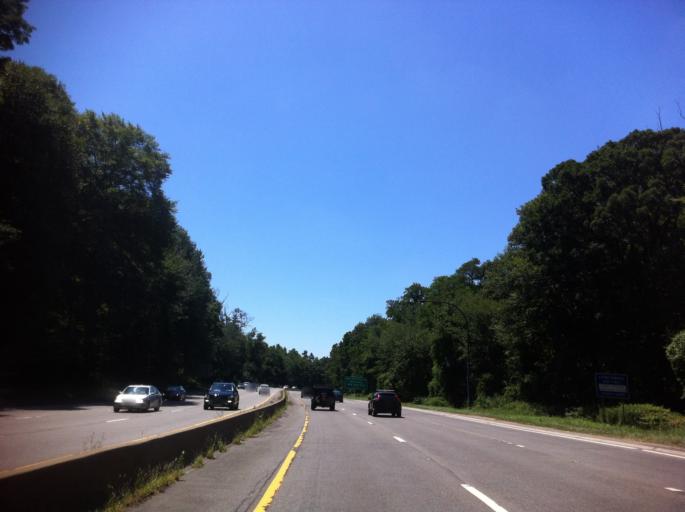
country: US
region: New York
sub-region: Nassau County
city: North Hills
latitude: 40.7727
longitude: -73.6741
